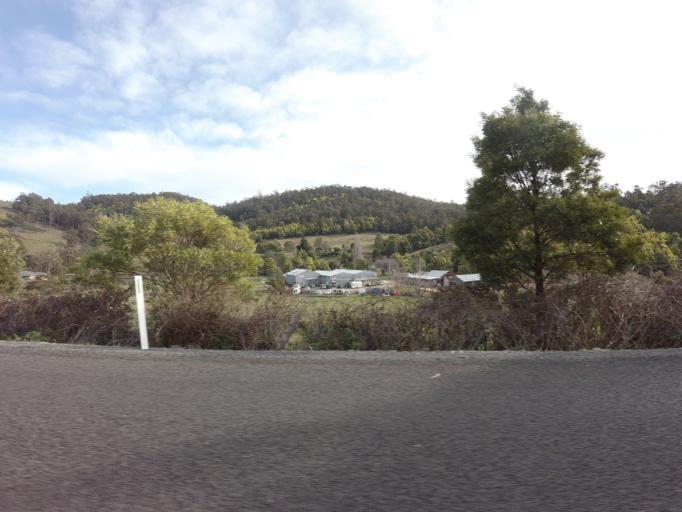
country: AU
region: Tasmania
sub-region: Kingborough
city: Margate
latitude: -42.9922
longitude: 147.1858
